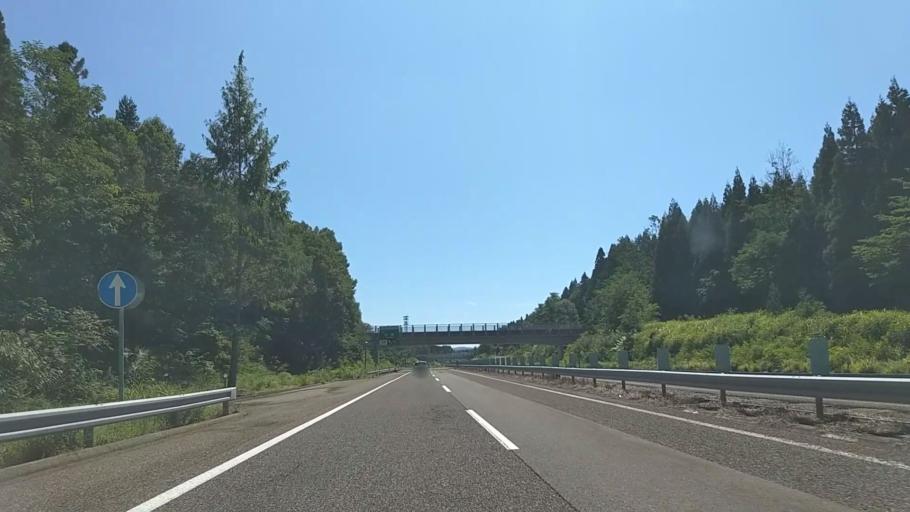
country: JP
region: Niigata
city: Arai
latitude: 36.9737
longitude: 138.2217
